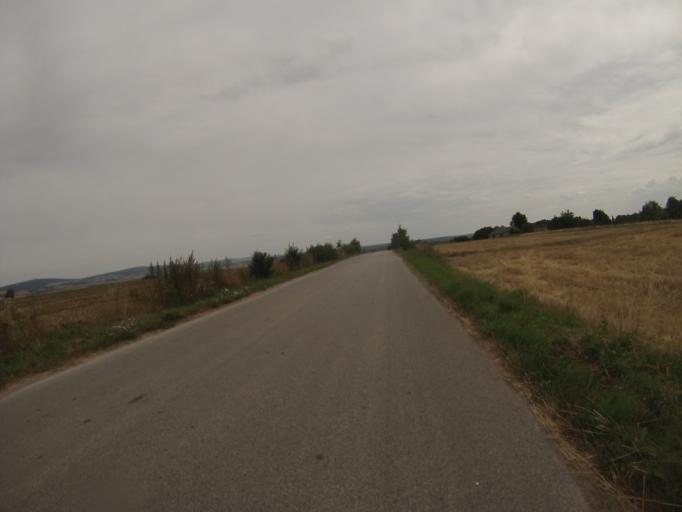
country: PL
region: Swietokrzyskie
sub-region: Powiat kielecki
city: Lagow
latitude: 50.7584
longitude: 21.0597
